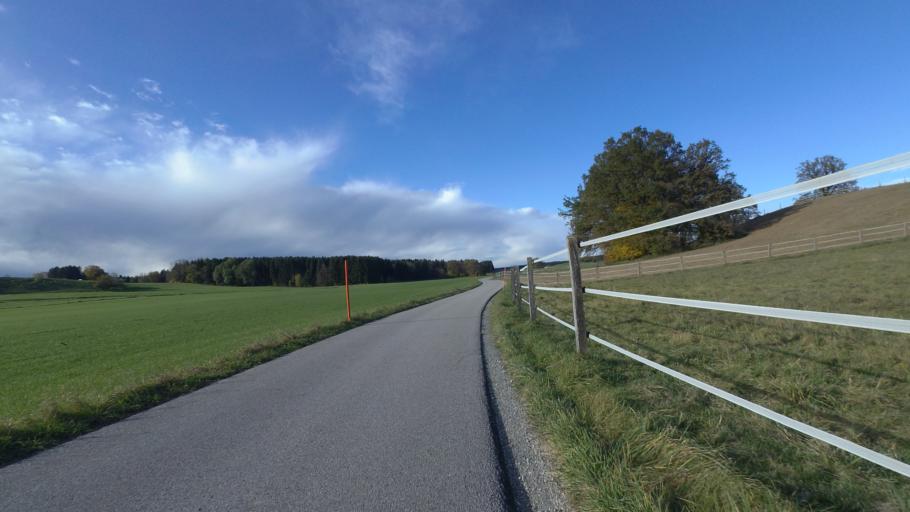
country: DE
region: Bavaria
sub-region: Upper Bavaria
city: Nussdorf
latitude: 47.9214
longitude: 12.5735
